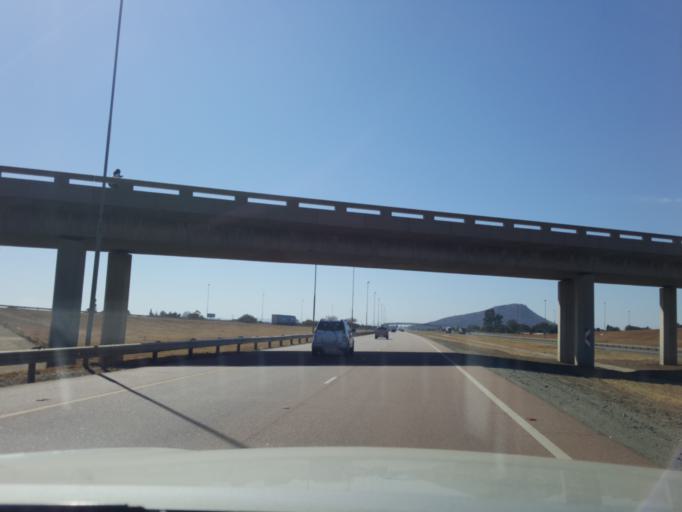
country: ZA
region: North-West
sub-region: Bojanala Platinum District Municipality
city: Brits
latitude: -25.7298
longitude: 27.6646
